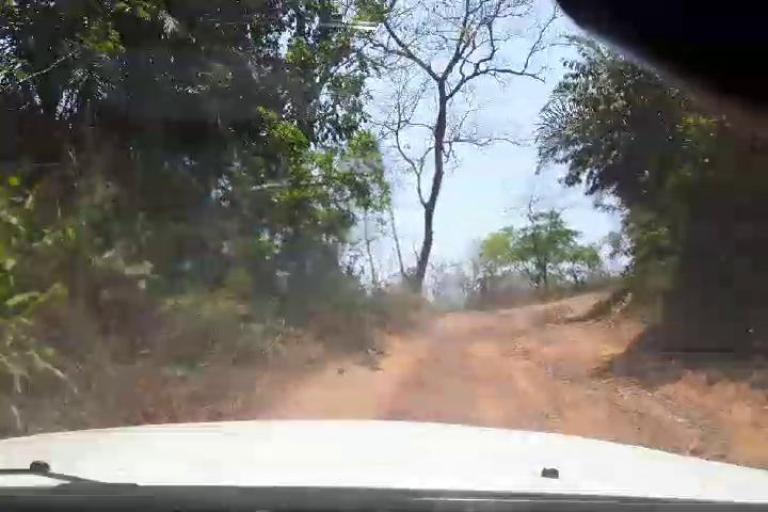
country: SL
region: Northern Province
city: Alikalia
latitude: 9.0756
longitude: -11.4759
